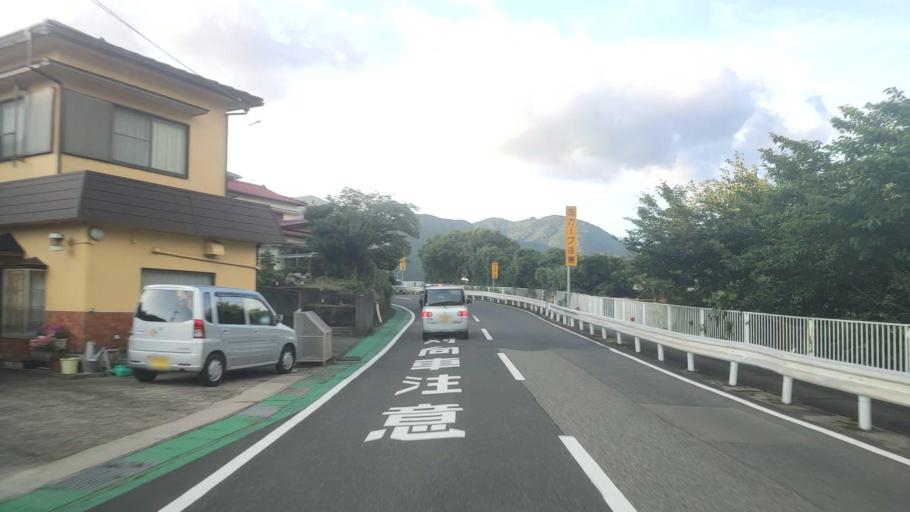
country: JP
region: Wakayama
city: Tanabe
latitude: 33.7209
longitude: 135.4815
